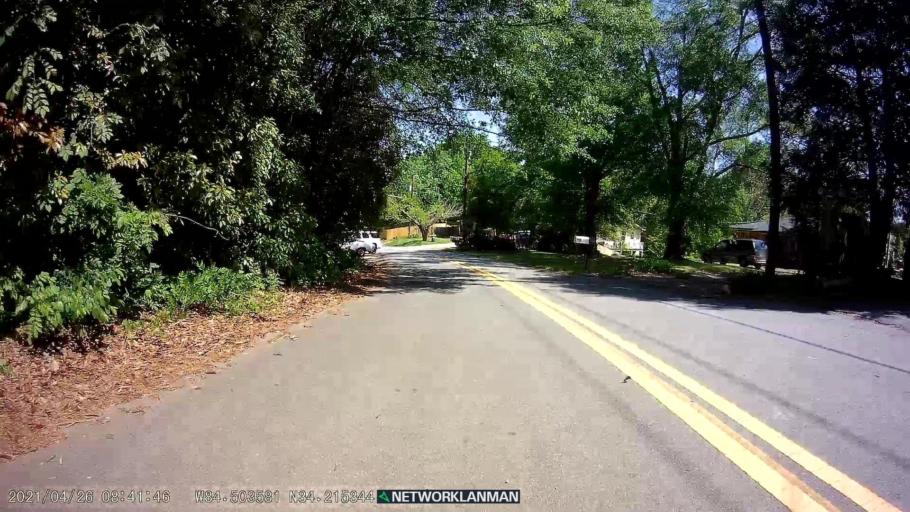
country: US
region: Georgia
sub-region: Cherokee County
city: Canton
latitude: 34.2153
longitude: -84.5037
